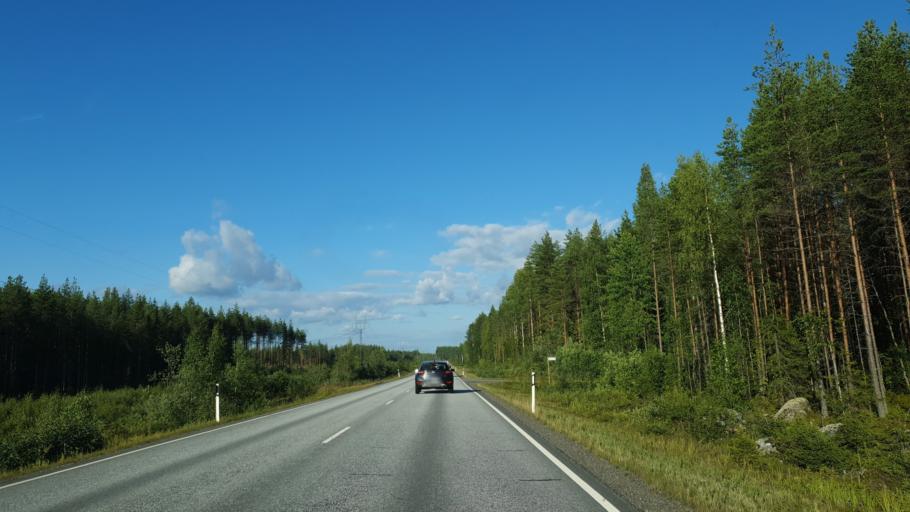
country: FI
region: North Karelia
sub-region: Joensuu
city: Outokumpu
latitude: 62.5311
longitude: 29.0883
